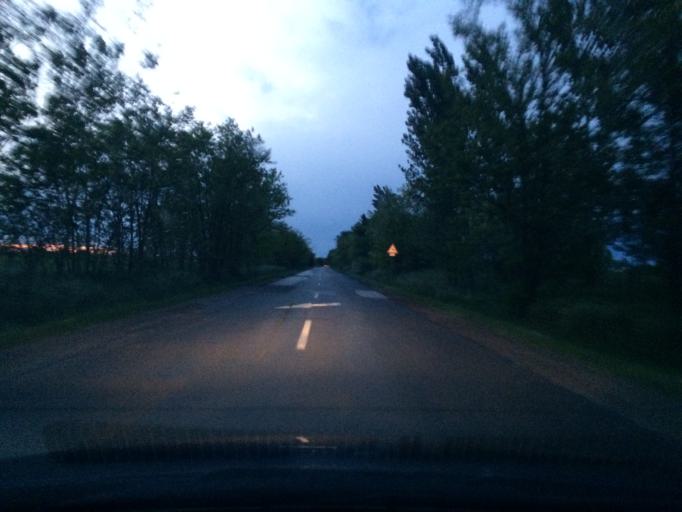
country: HU
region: Hajdu-Bihar
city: Hajdunanas
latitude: 47.8870
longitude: 21.4136
